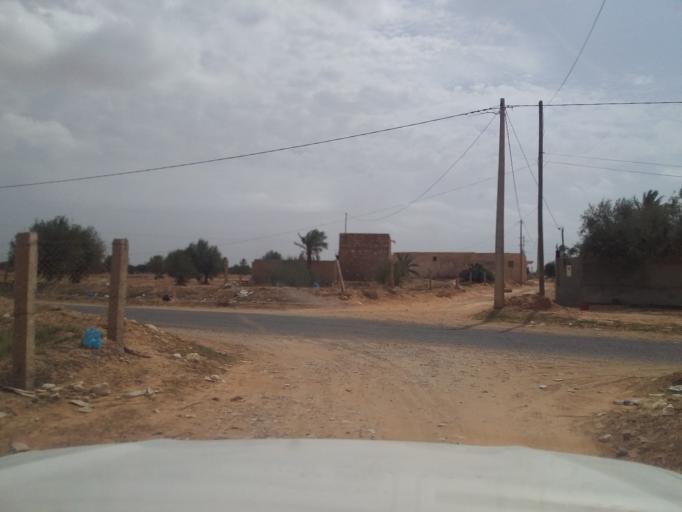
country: TN
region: Qabis
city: Matmata
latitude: 33.6177
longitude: 10.2634
